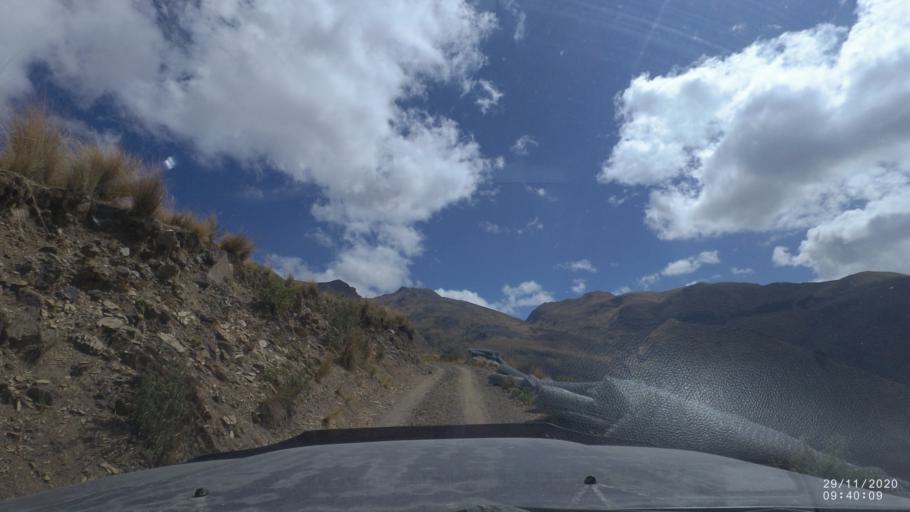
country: BO
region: Cochabamba
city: Cochabamba
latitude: -17.3036
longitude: -66.1804
